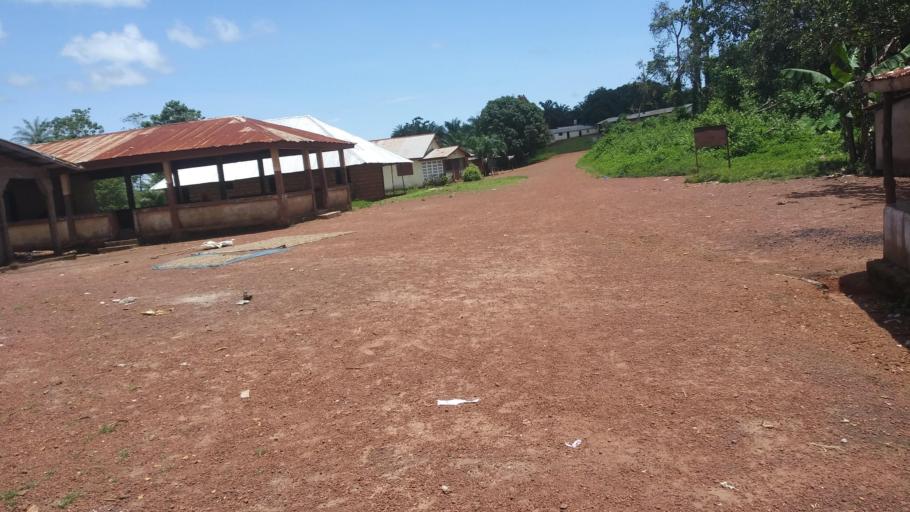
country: SL
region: Northern Province
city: Binkolo
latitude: 8.9016
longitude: -11.9894
